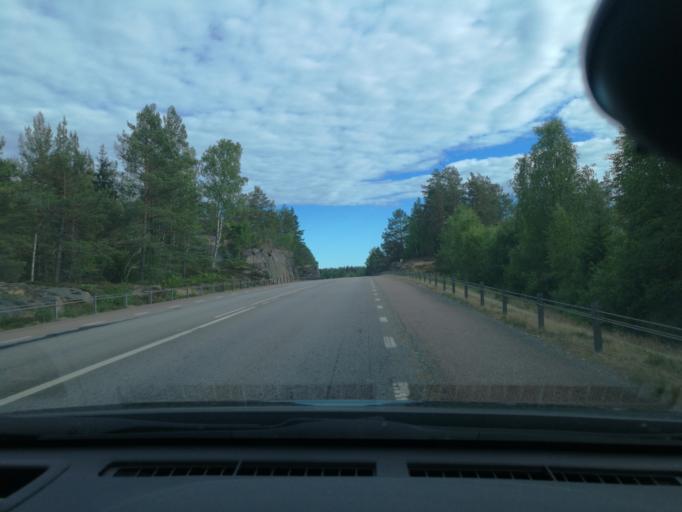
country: SE
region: Kalmar
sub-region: Vasterviks Kommun
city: Ankarsrum
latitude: 57.5941
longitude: 16.4834
